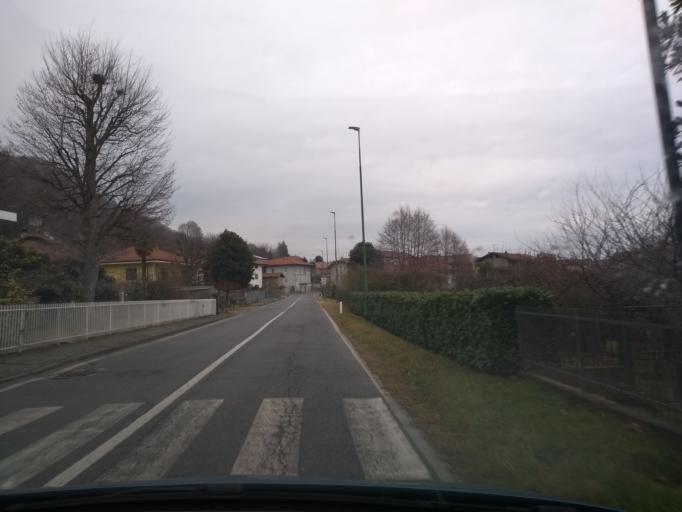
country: IT
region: Piedmont
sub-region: Provincia di Torino
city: Quagliuzzo
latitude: 45.4248
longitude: 7.7788
